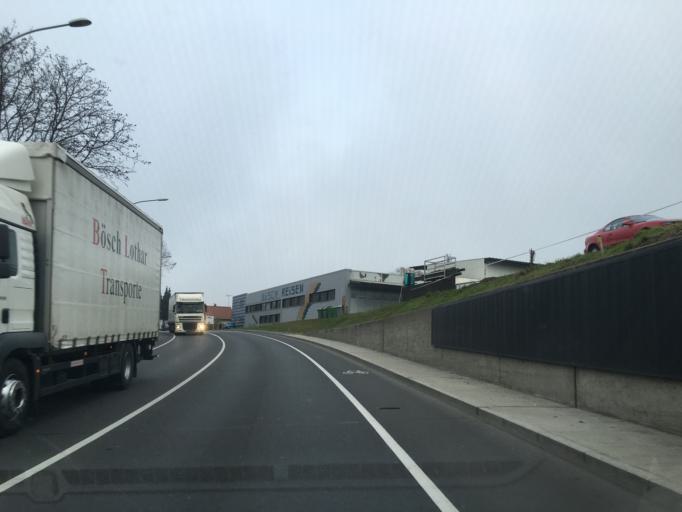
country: AT
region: Vorarlberg
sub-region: Politischer Bezirk Dornbirn
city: Lustenau
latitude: 47.4469
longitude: 9.6643
